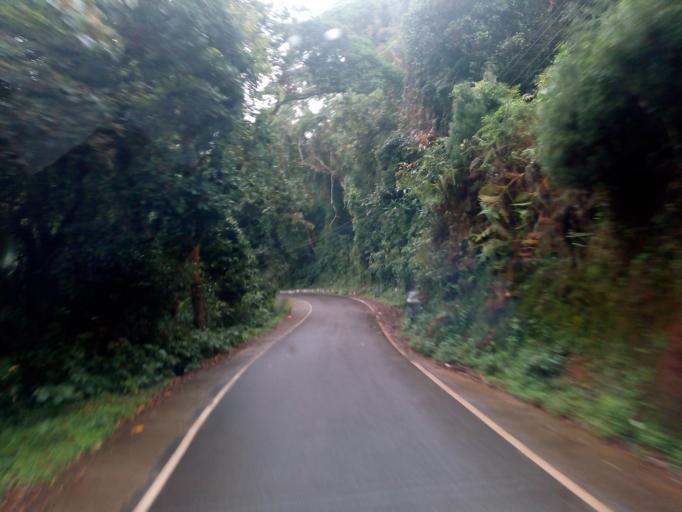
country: IN
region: Tamil Nadu
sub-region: Nilgiri
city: Wellington
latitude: 11.3624
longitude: 76.8365
